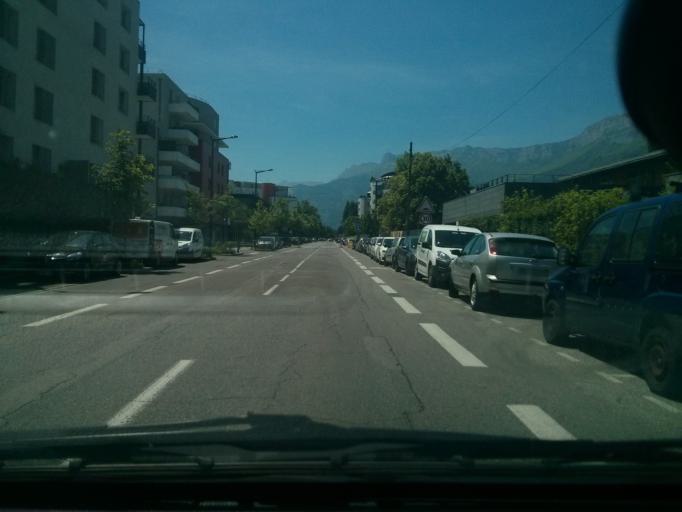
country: FR
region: Rhone-Alpes
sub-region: Departement de l'Isere
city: Grenoble
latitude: 45.1691
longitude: 5.7260
